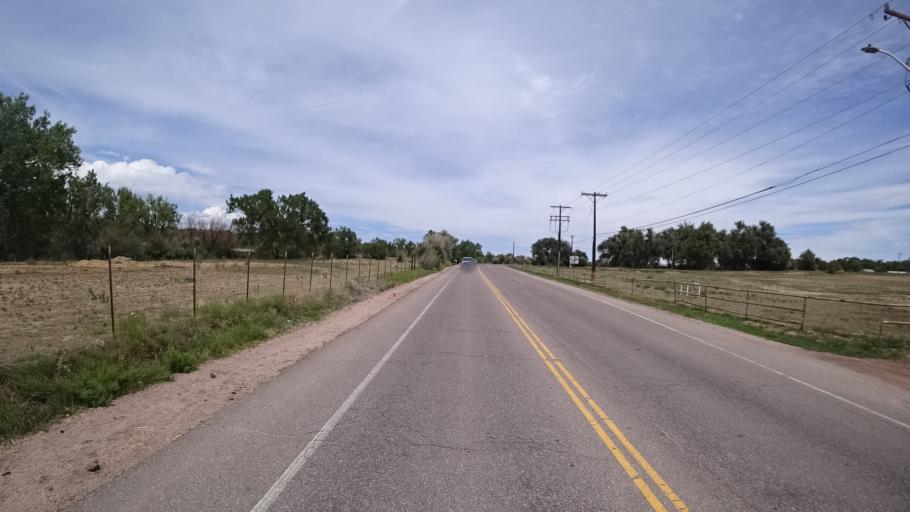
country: US
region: Colorado
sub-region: El Paso County
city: Fountain
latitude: 38.6830
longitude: -104.6876
